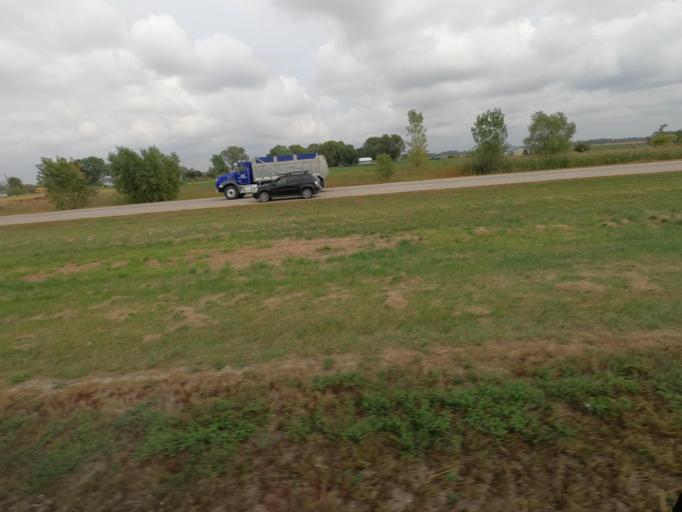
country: US
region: Iowa
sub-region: Wapello County
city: Ottumwa
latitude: 41.0565
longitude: -92.3741
